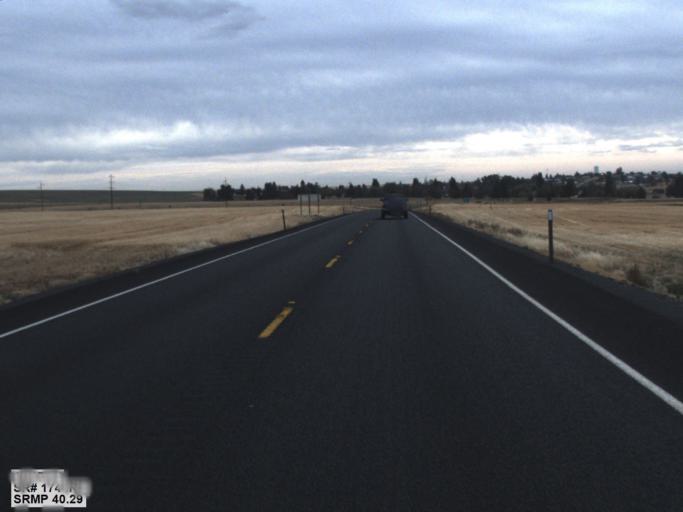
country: US
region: Washington
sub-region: Okanogan County
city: Coulee Dam
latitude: 47.7753
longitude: -118.7270
